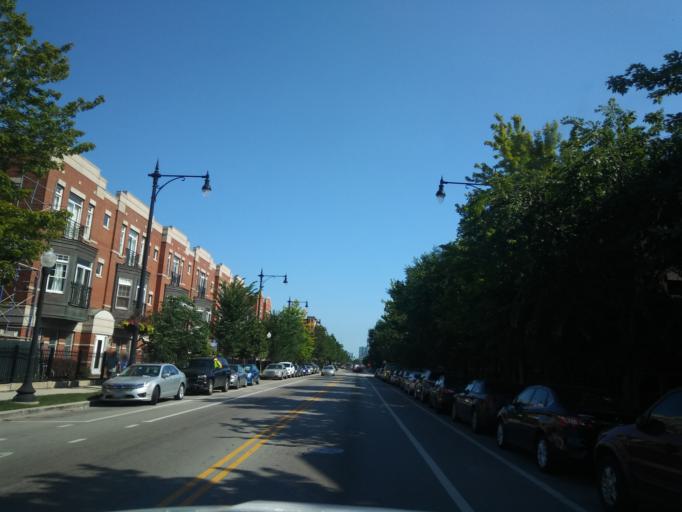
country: US
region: Illinois
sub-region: Cook County
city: Chicago
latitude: 41.8626
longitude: -87.6468
